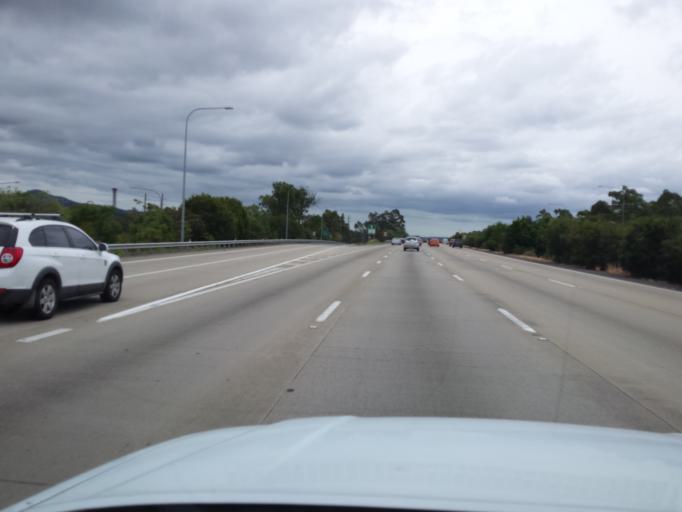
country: AU
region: Queensland
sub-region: Gold Coast
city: Upper Coomera
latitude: -27.9132
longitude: 153.3191
